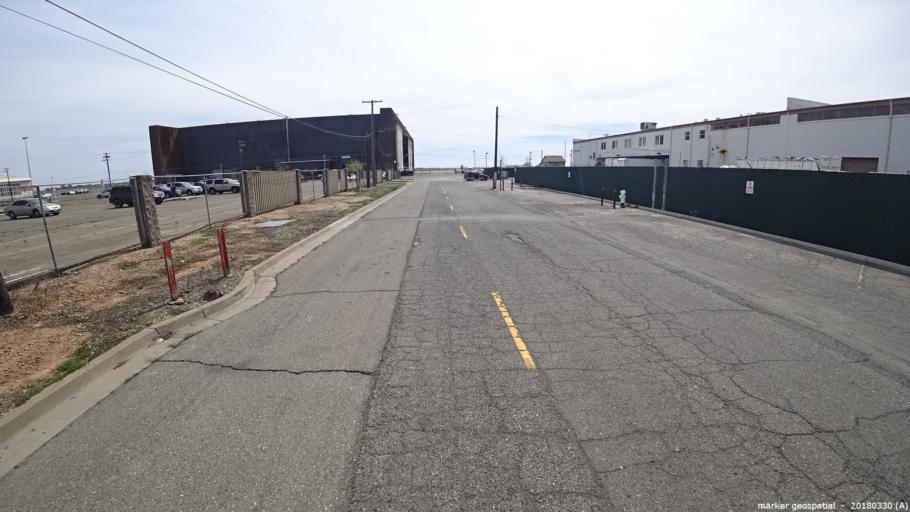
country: US
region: California
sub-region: Sacramento County
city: Rancho Cordova
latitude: 38.5651
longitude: -121.3052
